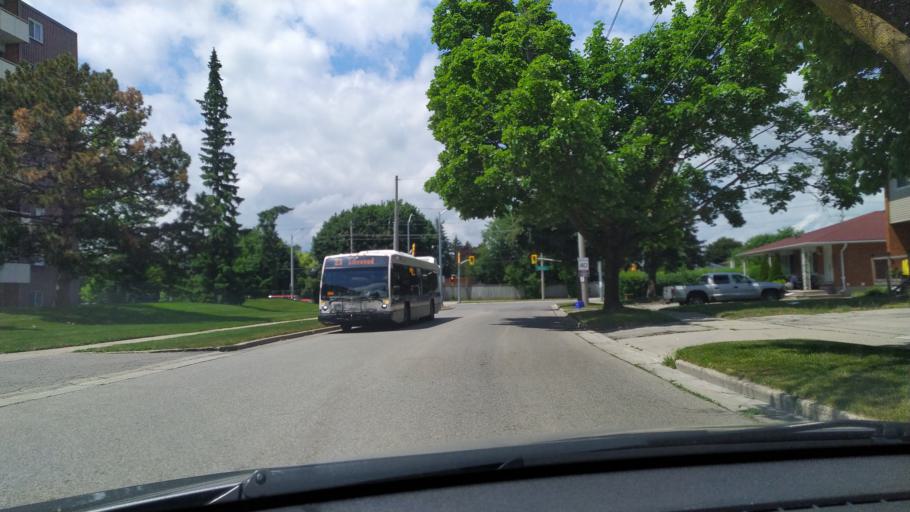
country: CA
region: Ontario
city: Kitchener
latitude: 43.4515
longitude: -80.4401
